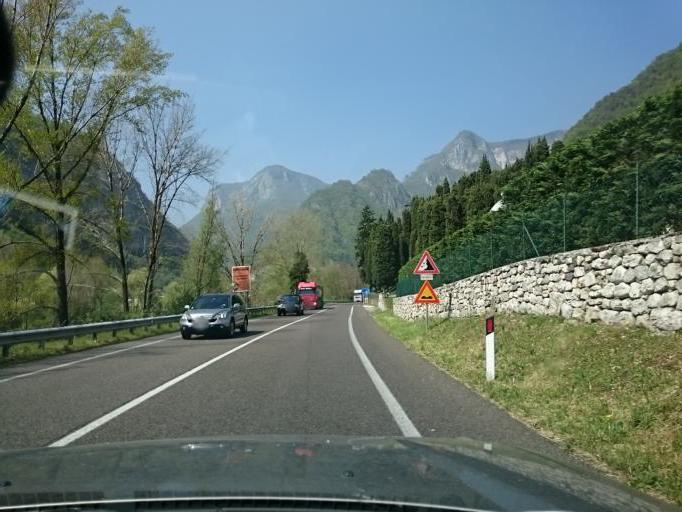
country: IT
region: Veneto
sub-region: Provincia di Vicenza
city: Valstagna
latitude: 45.8538
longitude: 11.6657
